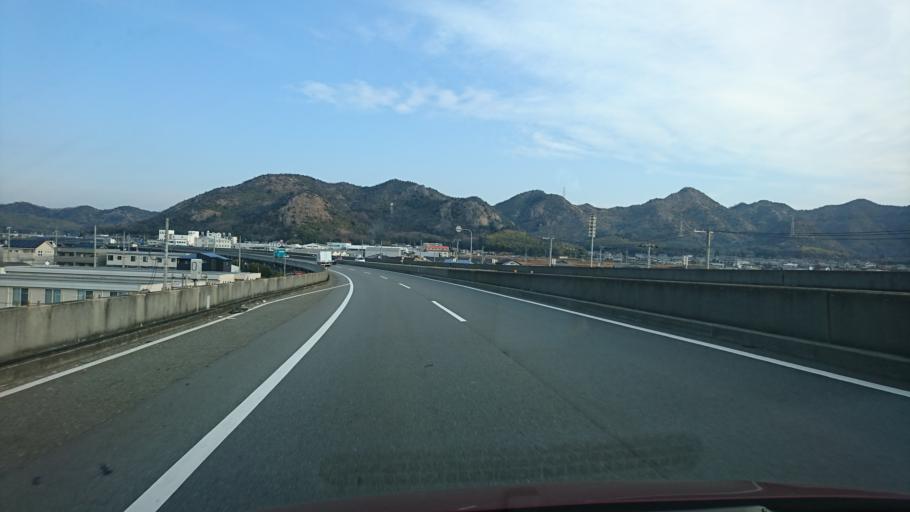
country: JP
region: Hyogo
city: Shirahamacho-usazakiminami
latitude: 34.8139
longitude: 134.7472
